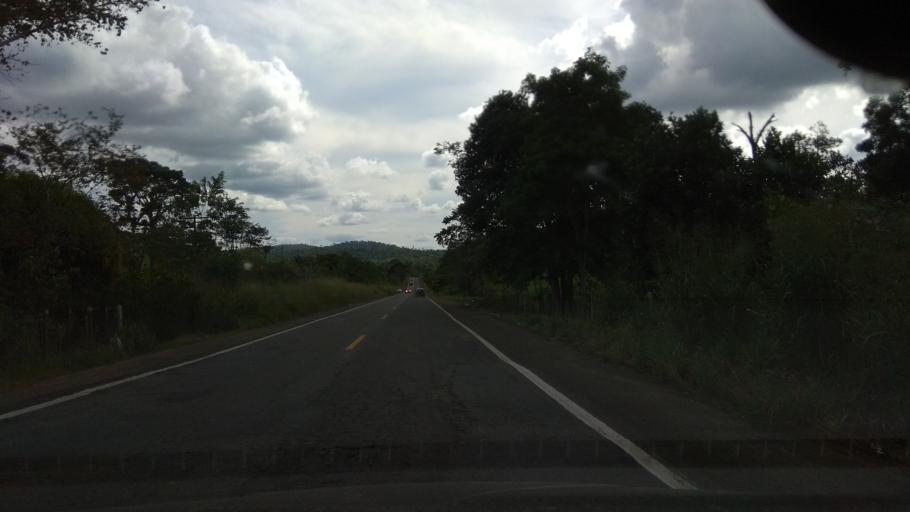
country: BR
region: Bahia
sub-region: Ubaitaba
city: Ubaitaba
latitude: -14.2611
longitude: -39.3439
